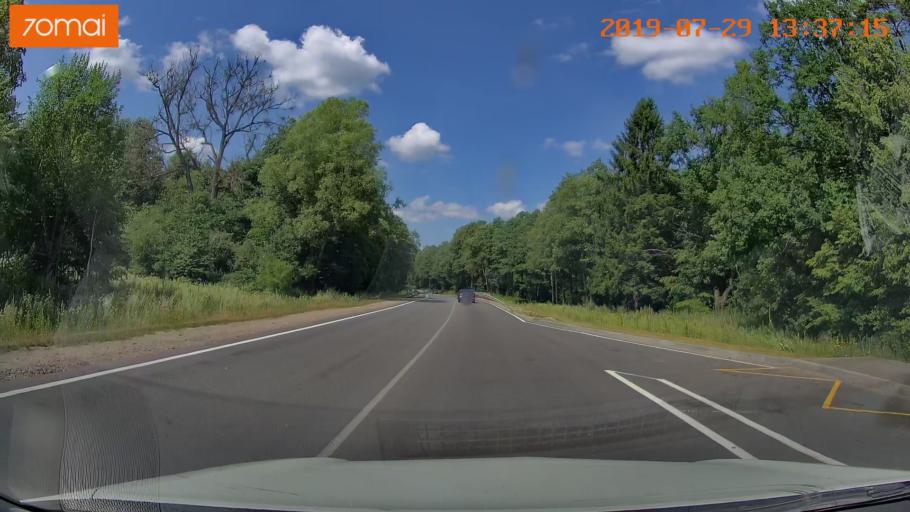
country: RU
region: Kaliningrad
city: Volochayevskoye
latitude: 54.7131
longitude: 20.1869
